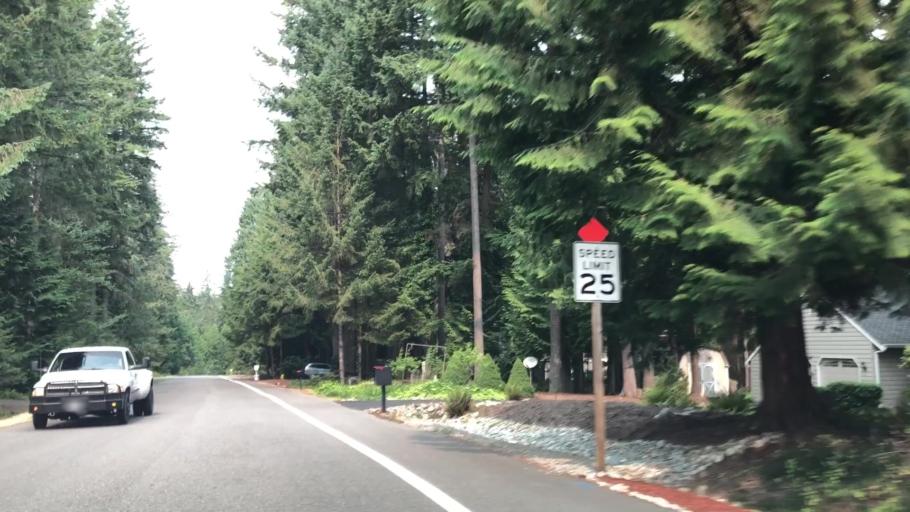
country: US
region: Washington
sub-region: King County
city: Cottage Lake
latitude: 47.7710
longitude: -122.0782
